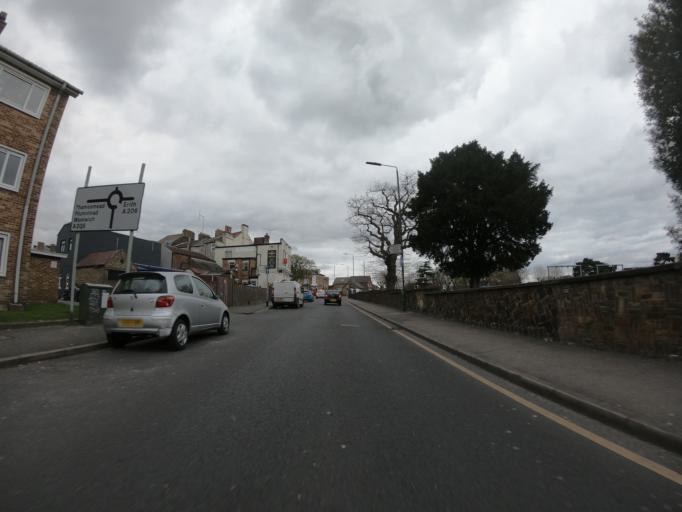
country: GB
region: England
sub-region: Greater London
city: Belvedere
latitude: 51.4835
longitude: 0.1437
